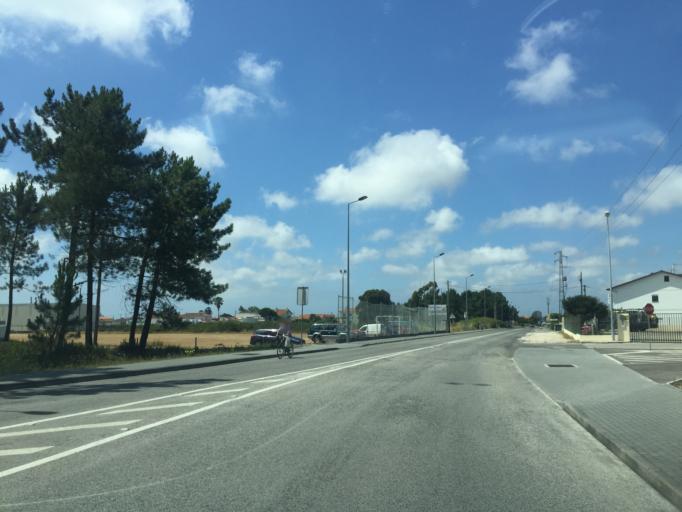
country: PT
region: Leiria
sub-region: Marinha Grande
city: Marinha Grande
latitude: 39.7272
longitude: -8.9289
